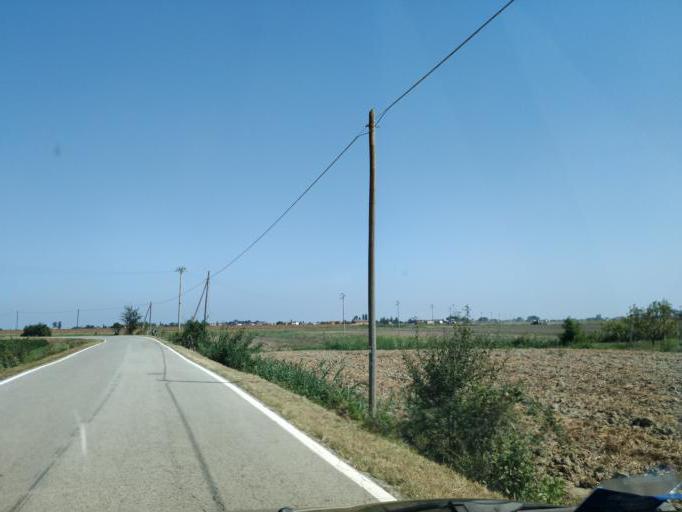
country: IT
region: Emilia-Romagna
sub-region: Provincia di Ferrara
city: Coccanile-Cesta
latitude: 44.8952
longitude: 11.9019
